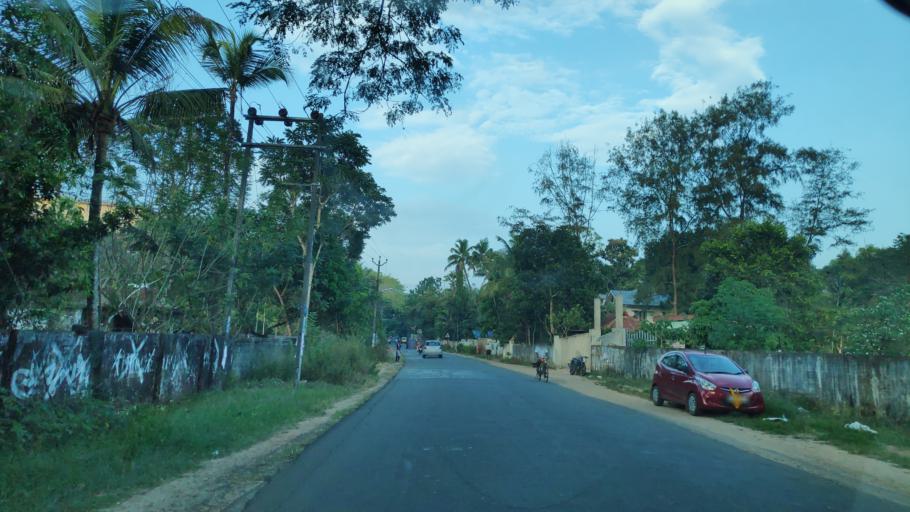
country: IN
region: Kerala
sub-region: Alappuzha
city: Shertallai
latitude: 9.6247
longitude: 76.3669
